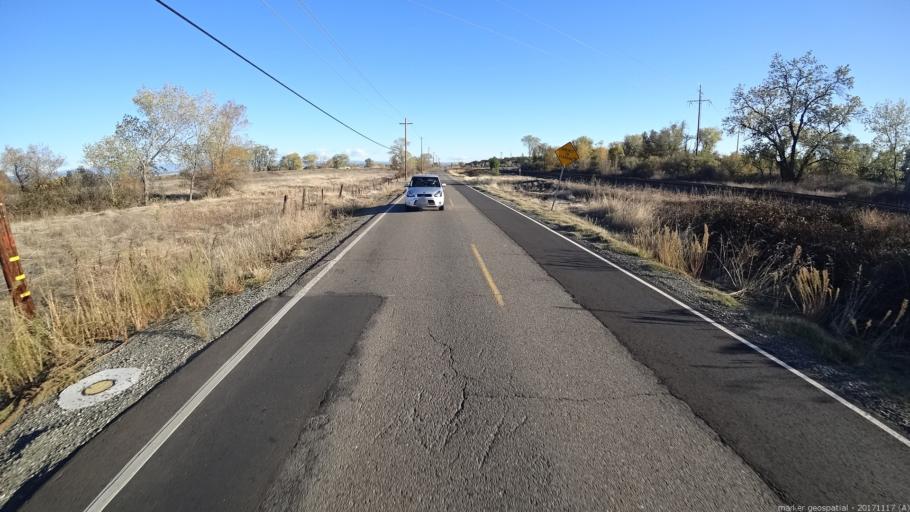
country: US
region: California
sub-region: Shasta County
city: Anderson
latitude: 40.4256
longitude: -122.2641
